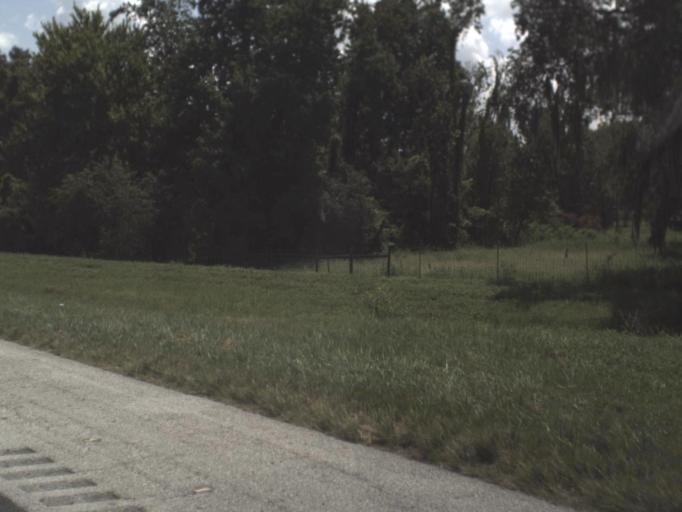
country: US
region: Florida
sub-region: Hillsborough County
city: Dover
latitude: 28.0214
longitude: -82.2516
